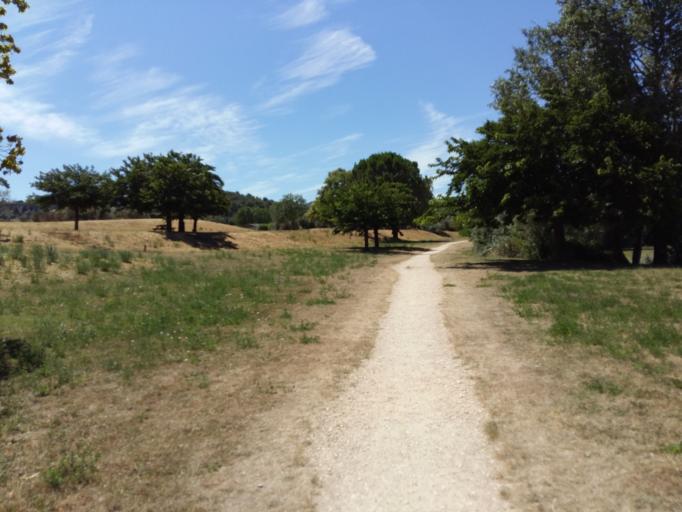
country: FR
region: Provence-Alpes-Cote d'Azur
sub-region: Departement du Vaucluse
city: Apt
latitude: 43.8910
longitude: 5.3807
